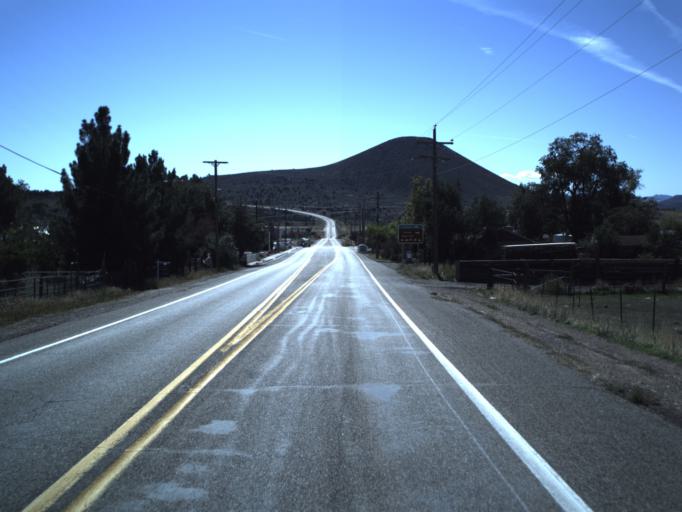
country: US
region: Utah
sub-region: Washington County
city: Ivins
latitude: 37.3405
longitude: -113.6933
